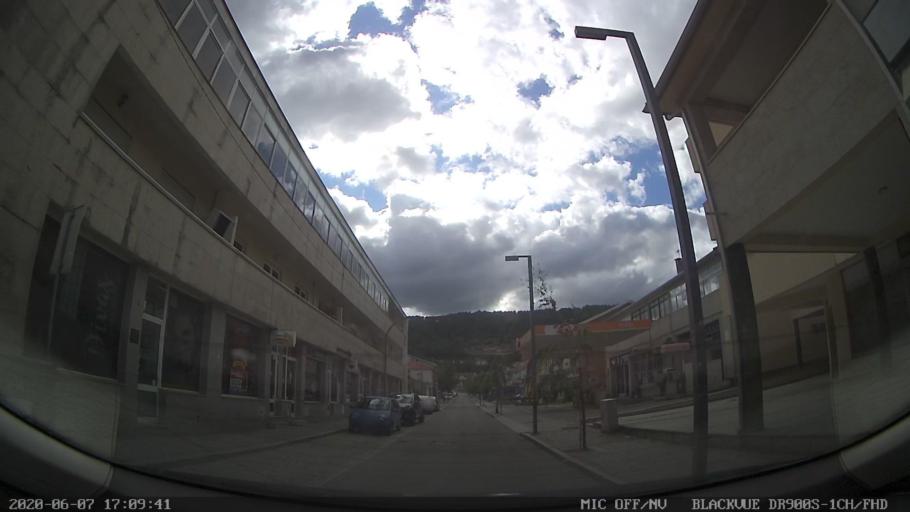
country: PT
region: Vila Real
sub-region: Vila Pouca de Aguiar
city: Vila Pouca de Aguiar
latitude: 41.5009
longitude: -7.6431
